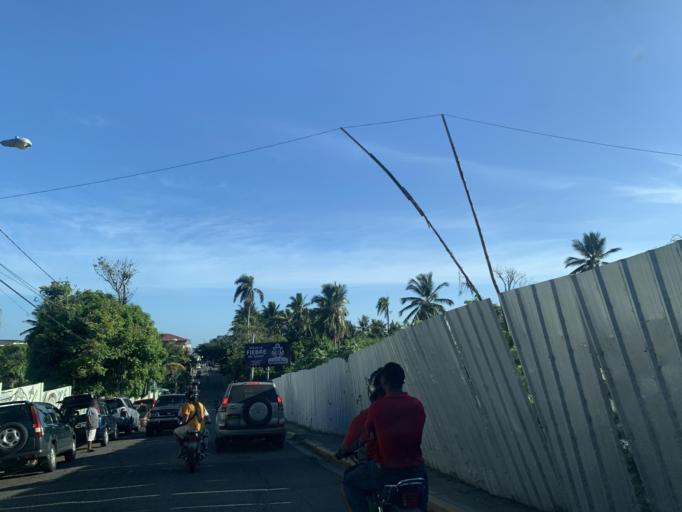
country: DO
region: Puerto Plata
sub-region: Puerto Plata
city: Puerto Plata
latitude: 19.7909
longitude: -70.6909
